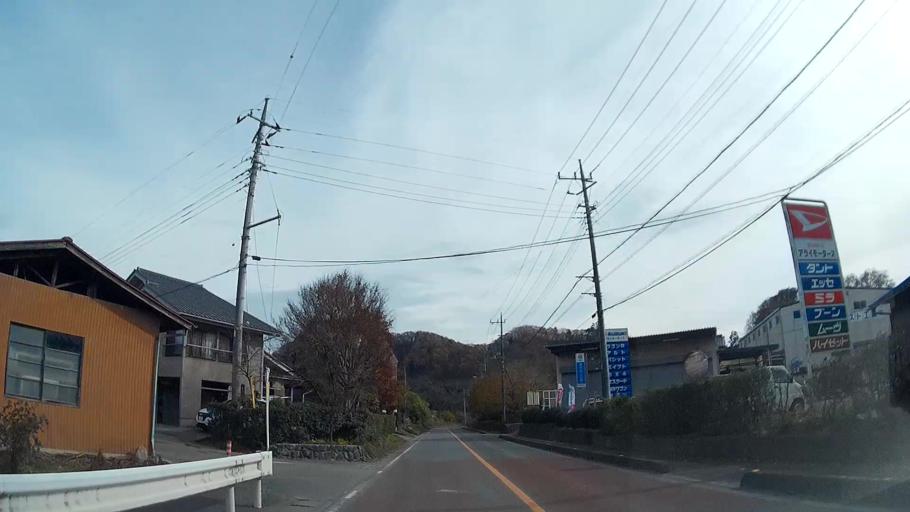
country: JP
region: Saitama
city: Chichibu
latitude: 36.0139
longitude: 139.0372
